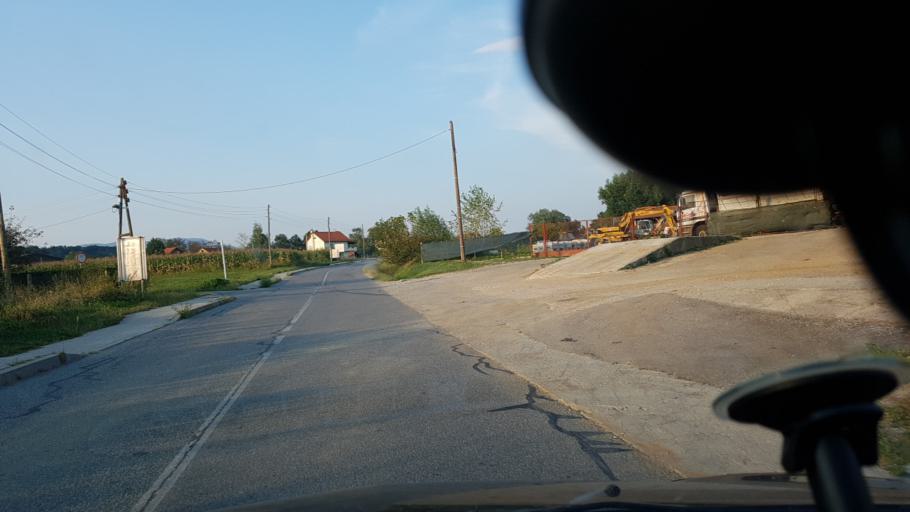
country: HR
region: Krapinsko-Zagorska
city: Selnica
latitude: 46.0536
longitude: 16.0387
